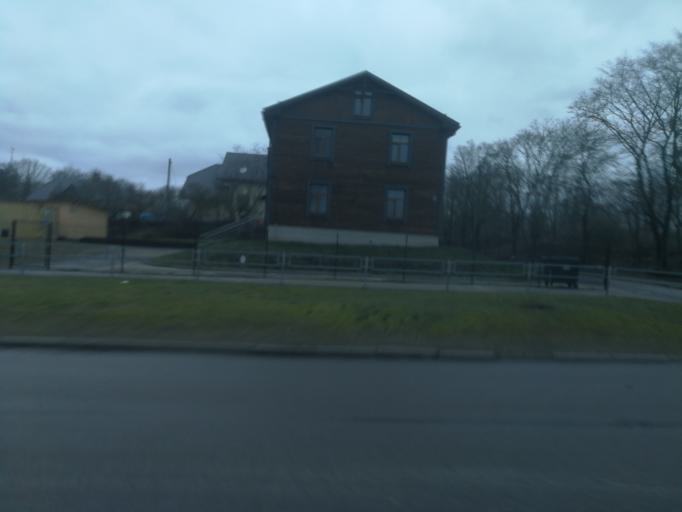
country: LV
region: Riga
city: Bolderaja
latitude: 57.0349
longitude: 24.1011
